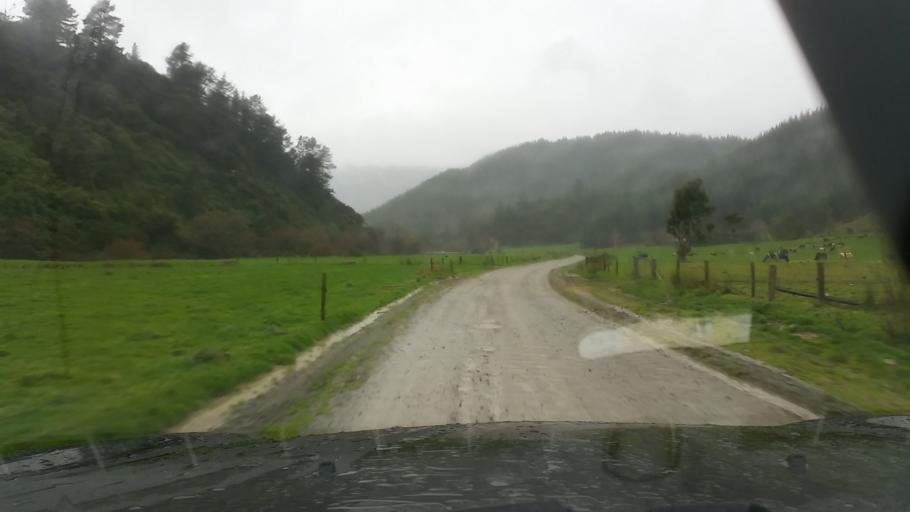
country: NZ
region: Marlborough
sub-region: Marlborough District
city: Picton
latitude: -41.3543
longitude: 173.9250
